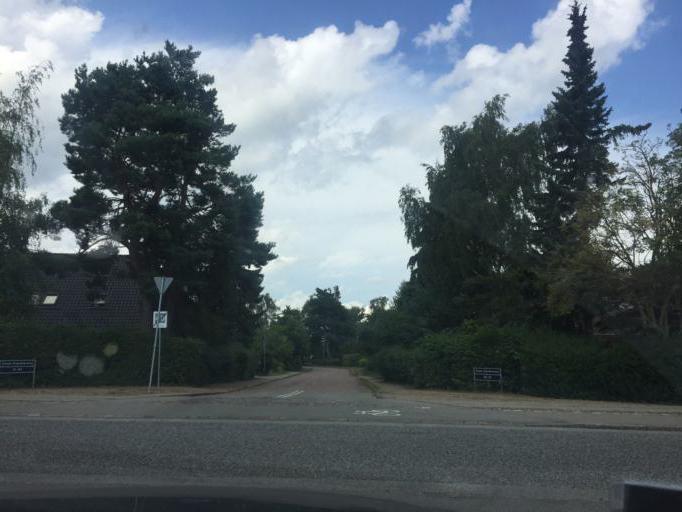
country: DK
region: Capital Region
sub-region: Rudersdal Kommune
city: Holte
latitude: 55.7914
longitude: 12.4521
